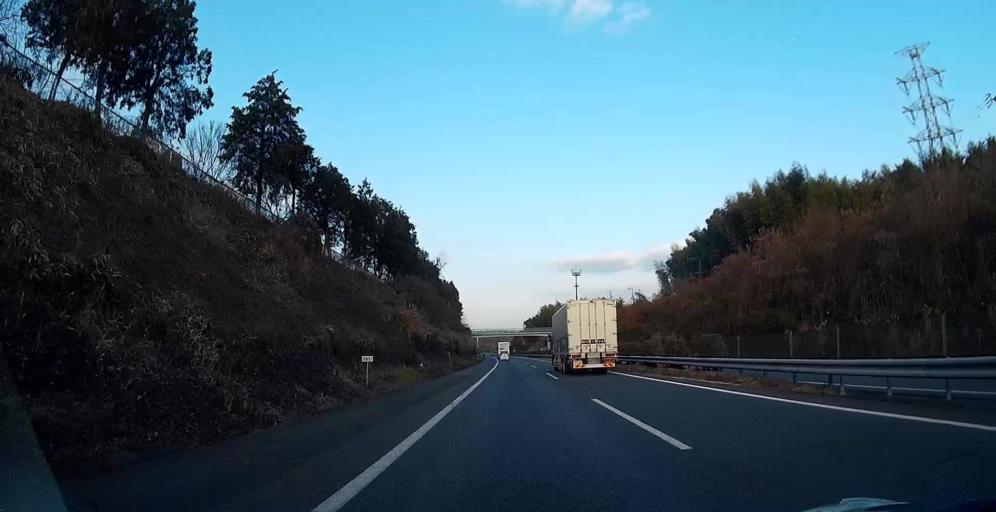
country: JP
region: Kumamoto
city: Uto
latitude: 32.6811
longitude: 130.7308
